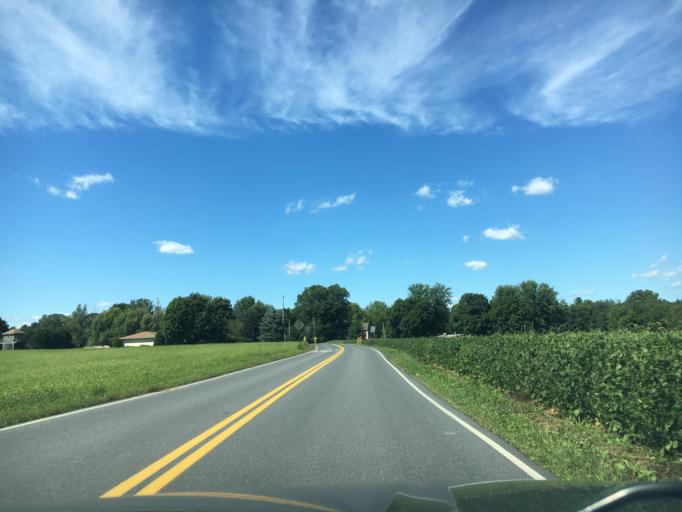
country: US
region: Pennsylvania
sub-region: Berks County
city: Topton
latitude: 40.5144
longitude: -75.6885
